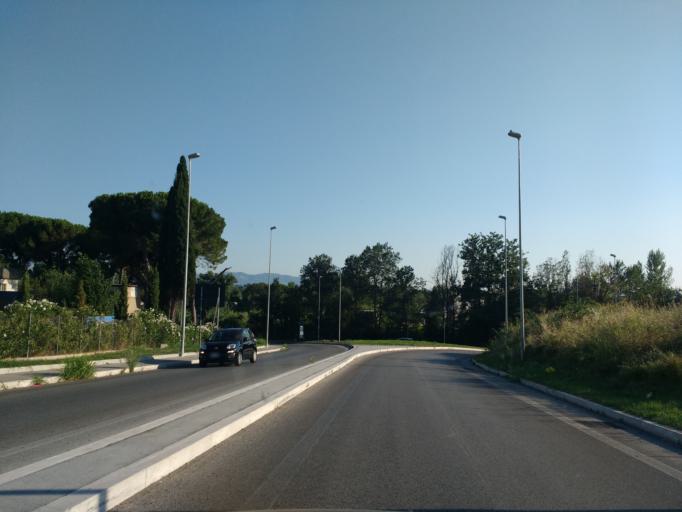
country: IT
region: Latium
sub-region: Citta metropolitana di Roma Capitale
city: Villanova
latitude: 41.9571
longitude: 12.7620
